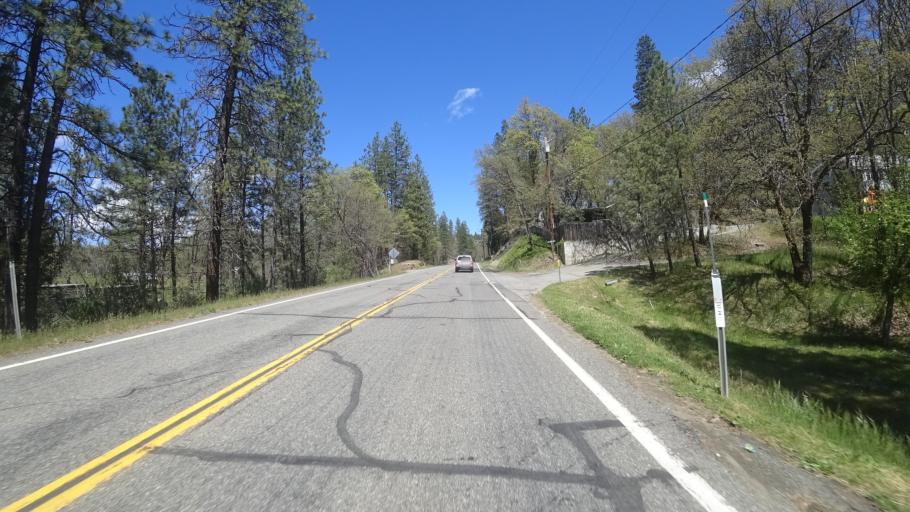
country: US
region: California
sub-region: Trinity County
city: Weaverville
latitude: 40.7512
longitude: -122.9174
